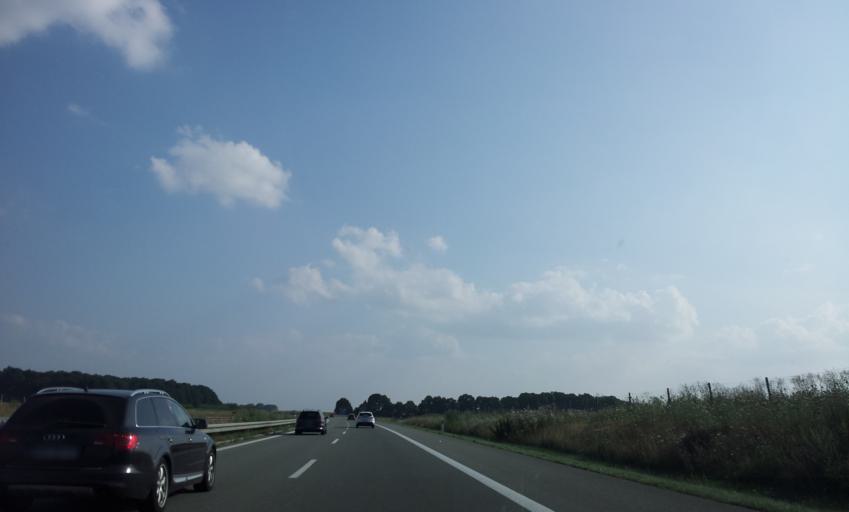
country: DE
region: Mecklenburg-Vorpommern
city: Neverin
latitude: 53.6321
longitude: 13.3674
